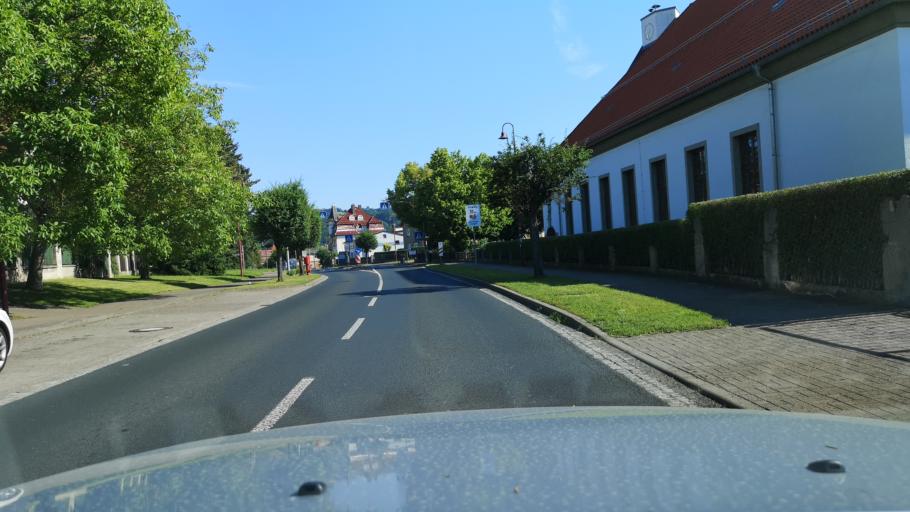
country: DE
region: Thuringia
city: Vacha
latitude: 50.8231
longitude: 10.0240
